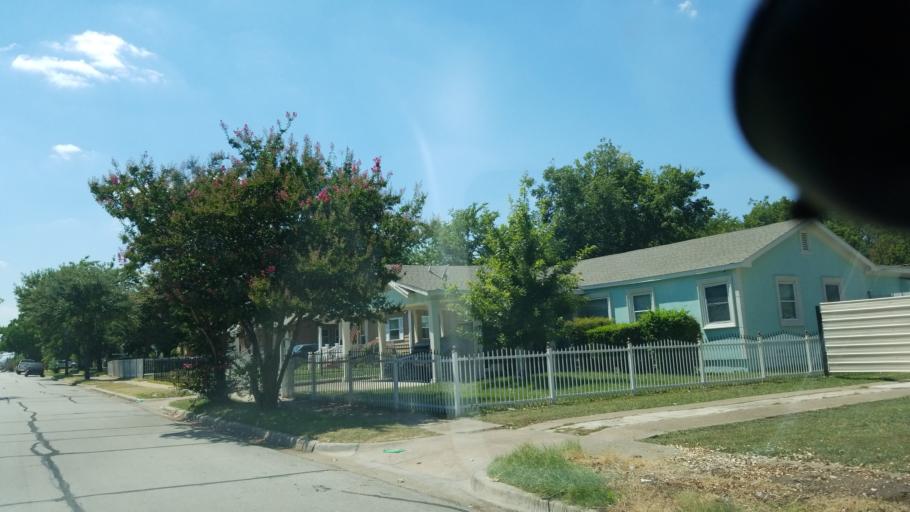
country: US
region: Texas
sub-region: Dallas County
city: Cockrell Hill
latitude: 32.7168
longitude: -96.8544
